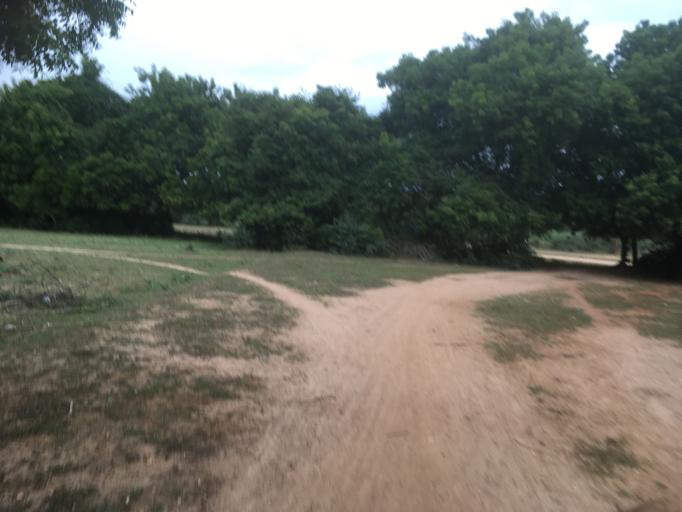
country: IN
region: Tamil Nadu
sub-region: Villupuram
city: Auroville
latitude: 12.0123
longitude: 79.8014
